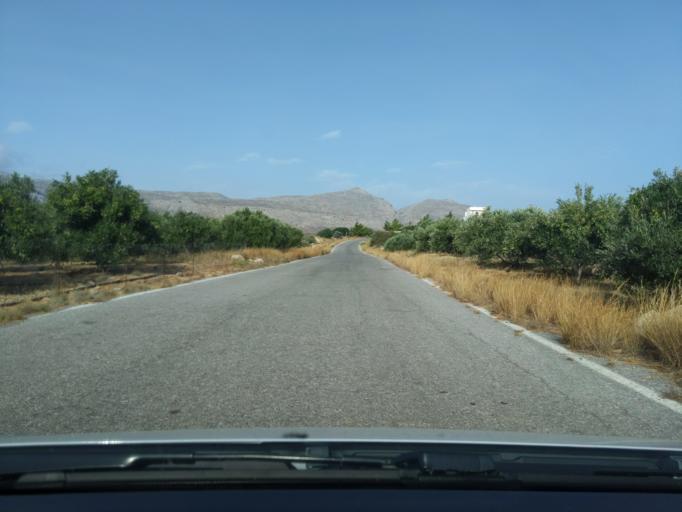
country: GR
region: Crete
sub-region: Nomos Lasithiou
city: Palekastro
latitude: 35.0847
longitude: 26.2463
